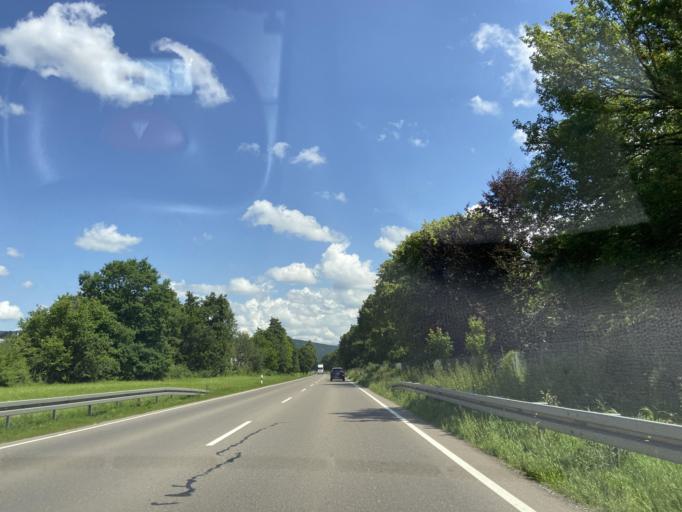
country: DE
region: Baden-Wuerttemberg
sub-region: Tuebingen Region
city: Albstadt
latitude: 48.2102
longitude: 8.9968
